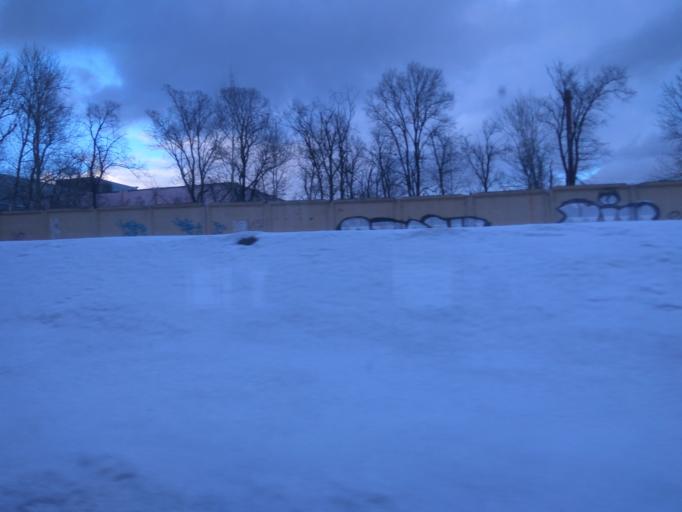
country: RU
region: Moscow
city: Tsaritsyno
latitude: 55.6266
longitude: 37.6286
